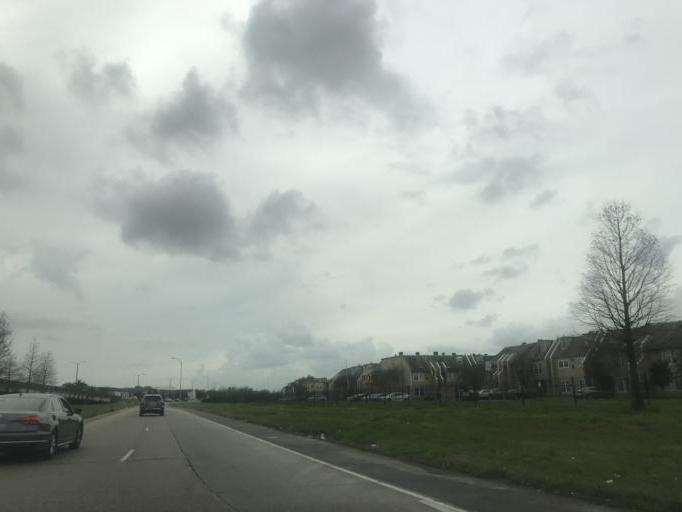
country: US
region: Louisiana
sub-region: Saint Bernard Parish
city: Arabi
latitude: 30.0303
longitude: -89.9944
